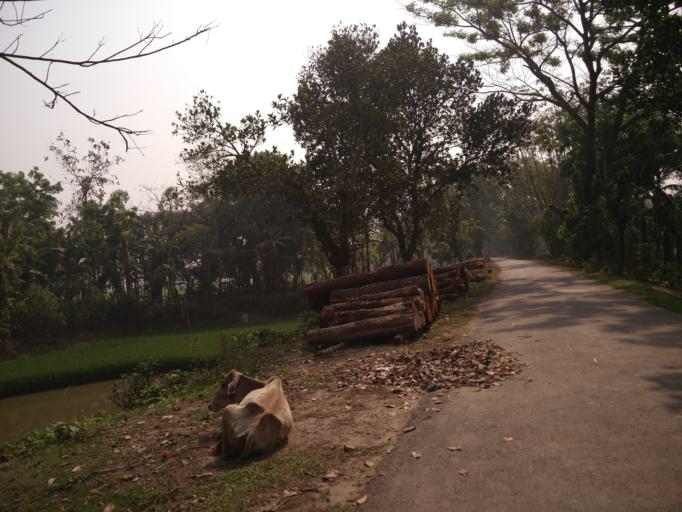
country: BD
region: Dhaka
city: Muktagacha
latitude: 24.9094
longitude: 90.1618
